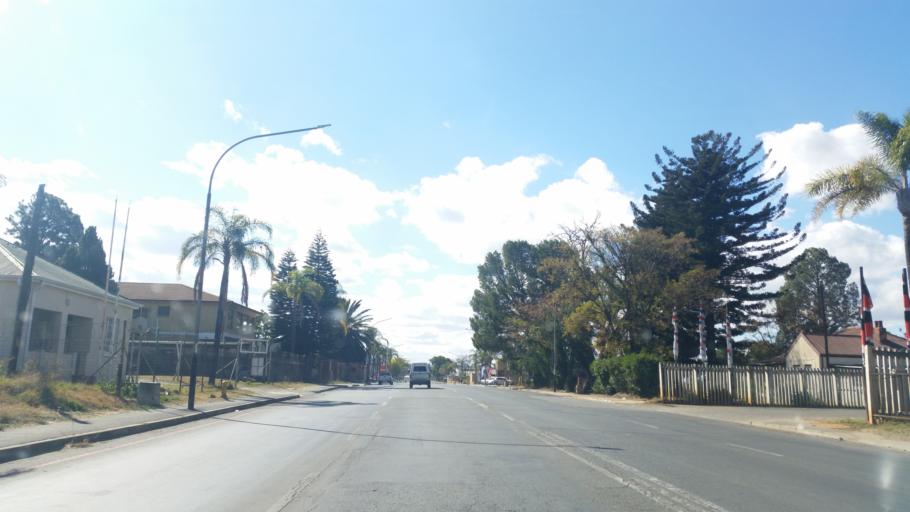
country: ZA
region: KwaZulu-Natal
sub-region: uThukela District Municipality
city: Ladysmith
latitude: -28.5685
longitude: 29.7769
